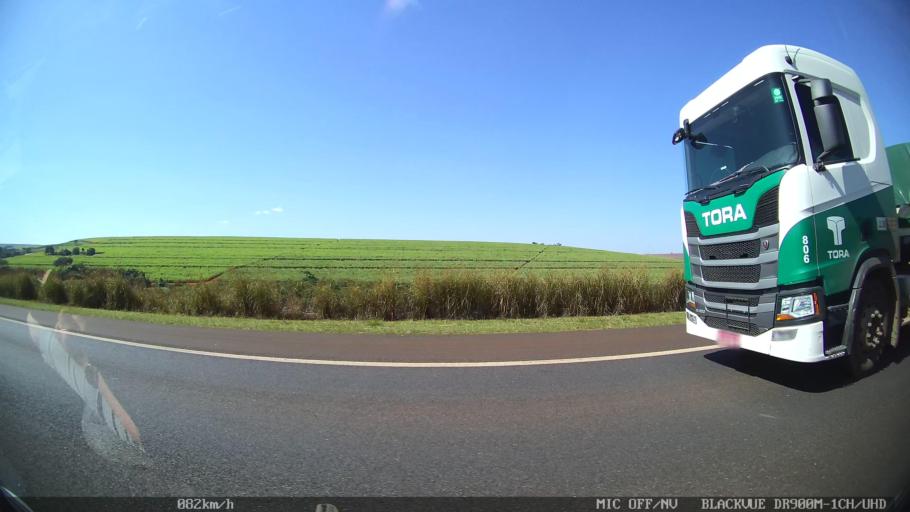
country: BR
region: Sao Paulo
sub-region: Franca
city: Franca
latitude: -20.7083
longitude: -47.5039
